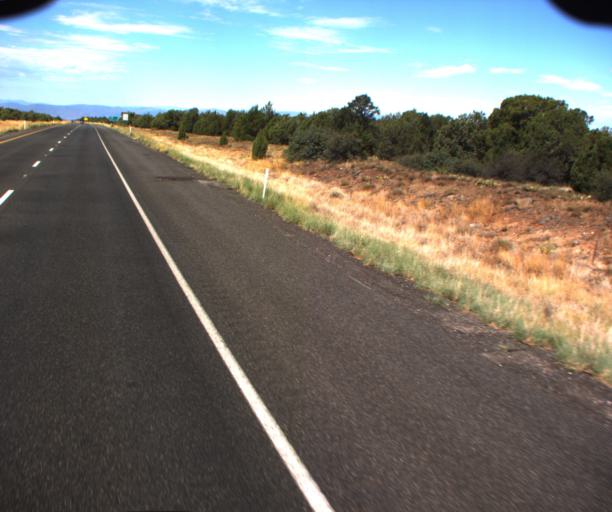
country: US
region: Arizona
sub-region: Yavapai County
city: Village of Oak Creek (Big Park)
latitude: 34.7585
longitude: -111.6647
